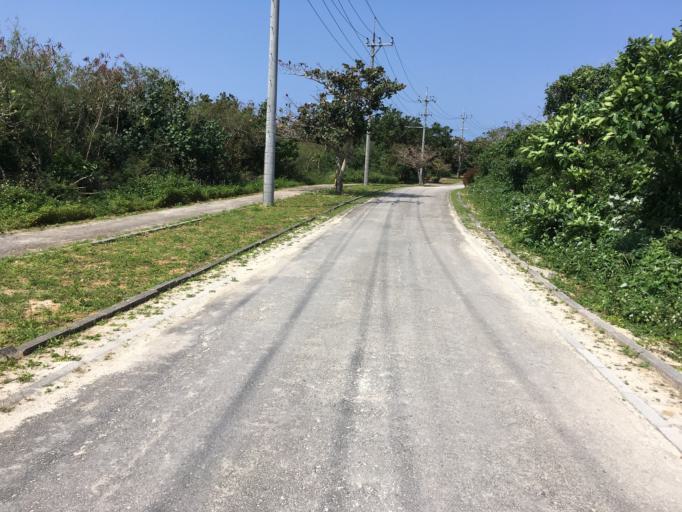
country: JP
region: Okinawa
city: Ishigaki
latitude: 24.3308
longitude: 124.0804
